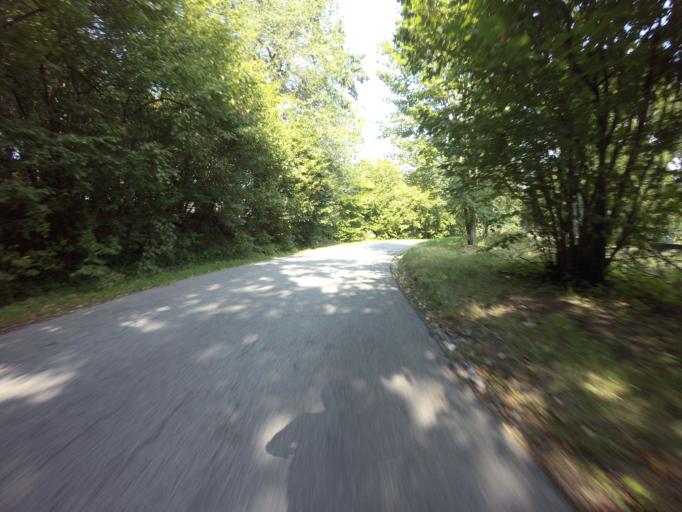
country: CZ
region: Jihocesky
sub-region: Okres Cesky Krumlov
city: Vyssi Brod
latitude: 48.6475
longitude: 14.3588
